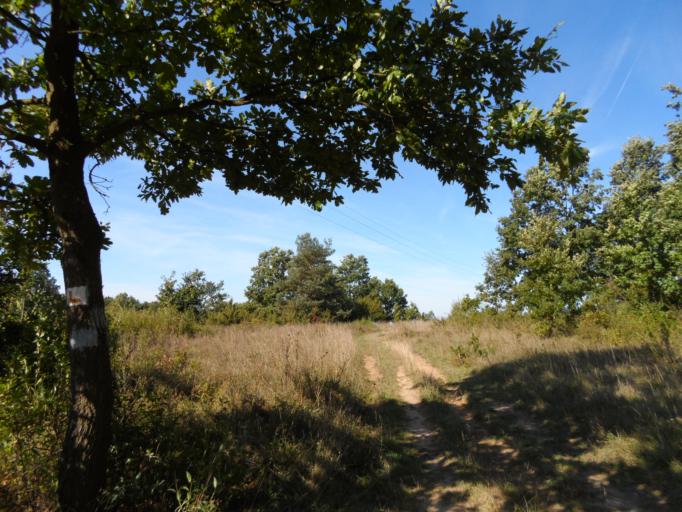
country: HU
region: Veszprem
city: Ajka
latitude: 47.2262
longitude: 17.5579
